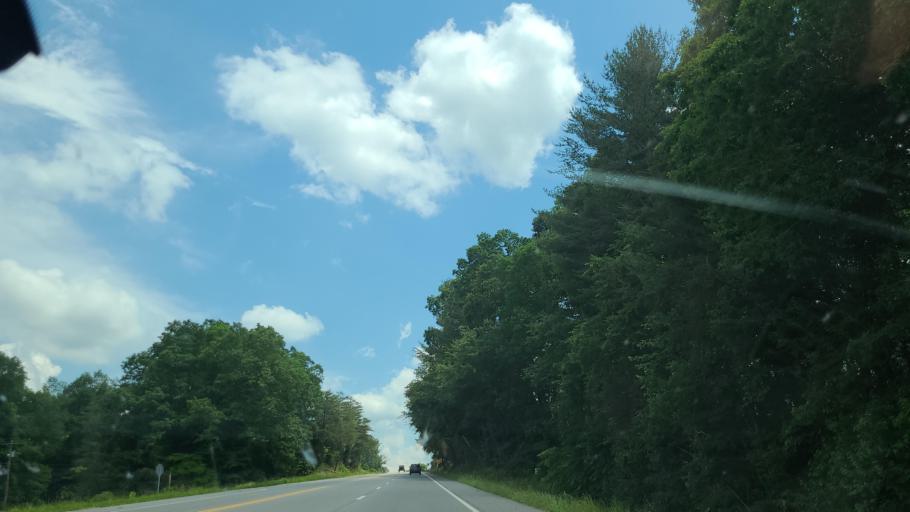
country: US
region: Tennessee
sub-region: Cumberland County
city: Crossville
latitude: 35.9097
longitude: -84.9899
